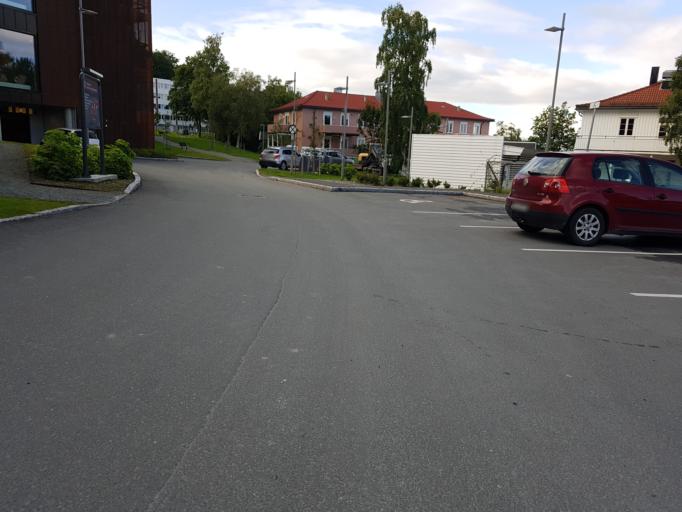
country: NO
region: Sor-Trondelag
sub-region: Trondheim
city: Trondheim
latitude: 63.4288
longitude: 10.4409
